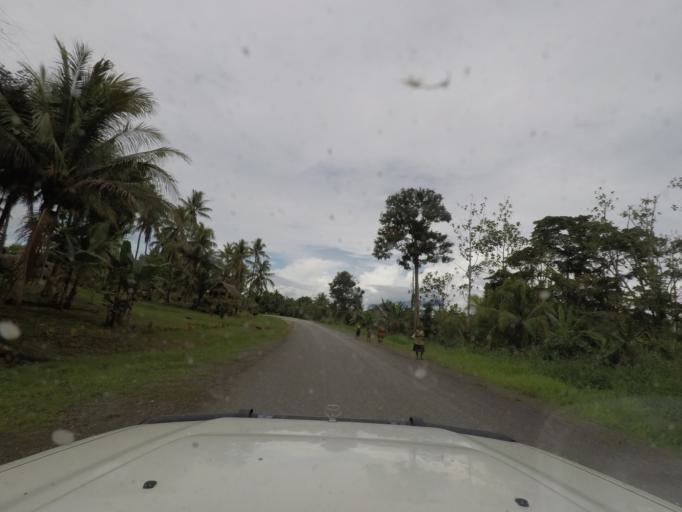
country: PG
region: Eastern Highlands
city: Goroka
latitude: -5.6723
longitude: 145.4995
